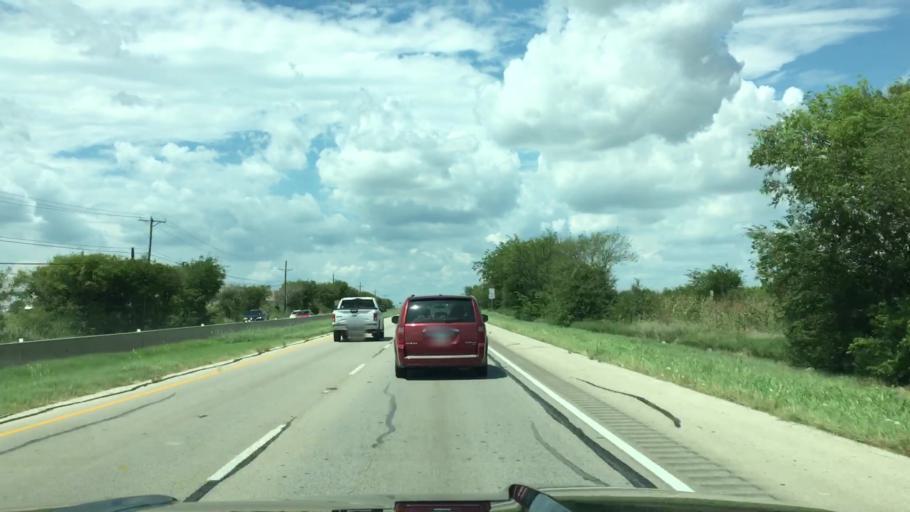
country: US
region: Texas
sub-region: Tarrant County
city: Saginaw
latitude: 32.8912
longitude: -97.3906
